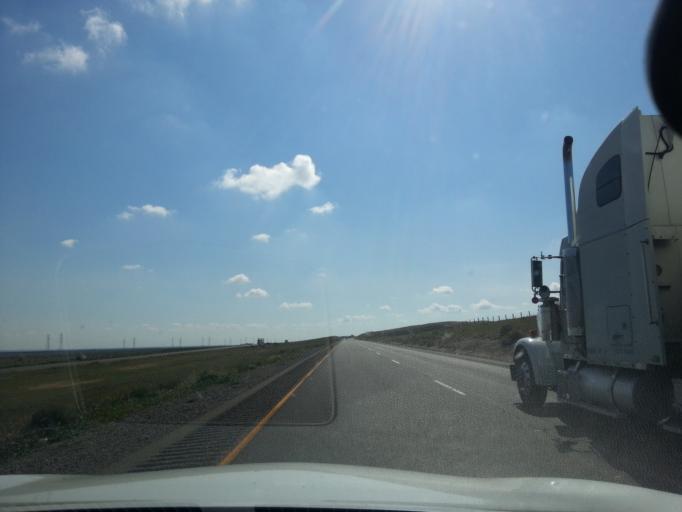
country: US
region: California
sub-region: Fresno County
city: Mendota
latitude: 36.5002
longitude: -120.4541
